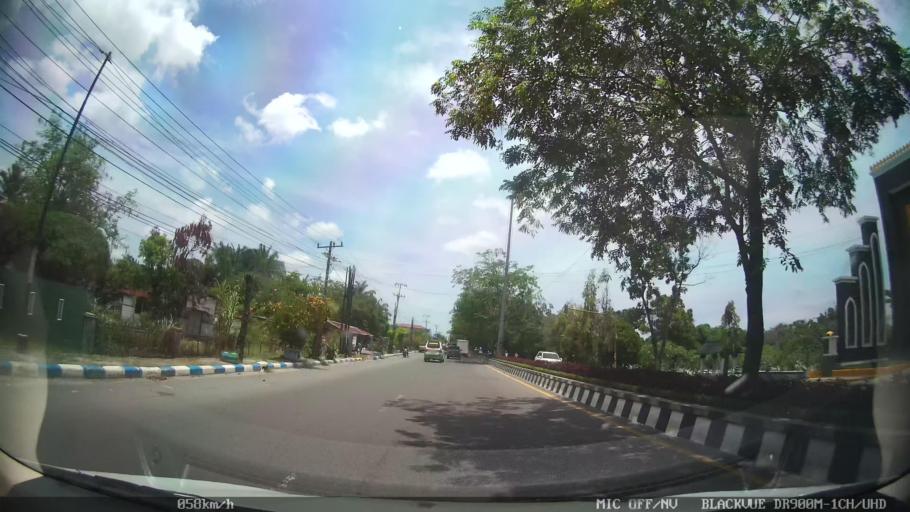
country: ID
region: North Sumatra
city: Percut
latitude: 3.5520
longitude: 98.8690
